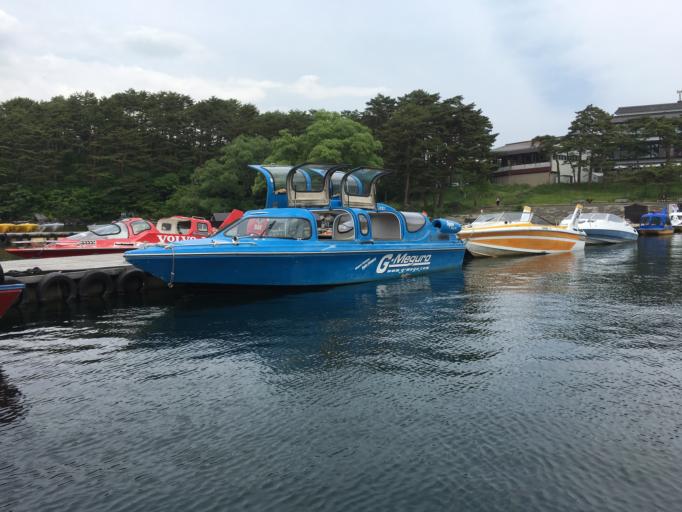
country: JP
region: Fukushima
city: Inawashiro
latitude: 37.6534
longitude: 140.0634
